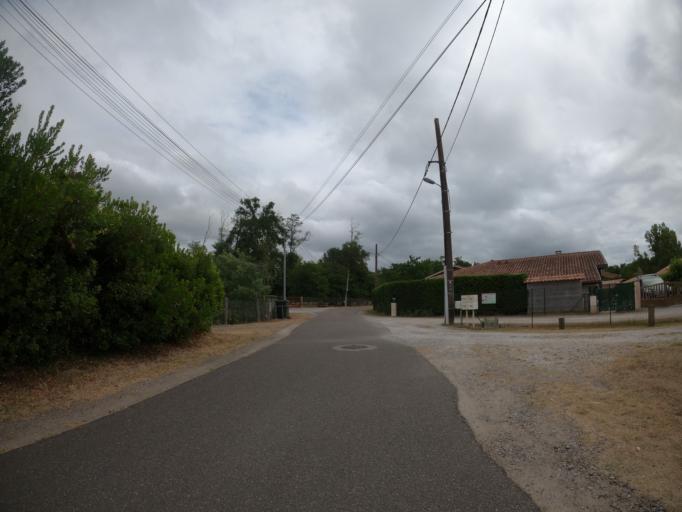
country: FR
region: Aquitaine
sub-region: Departement des Landes
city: Leon
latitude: 43.8849
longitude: -1.3031
